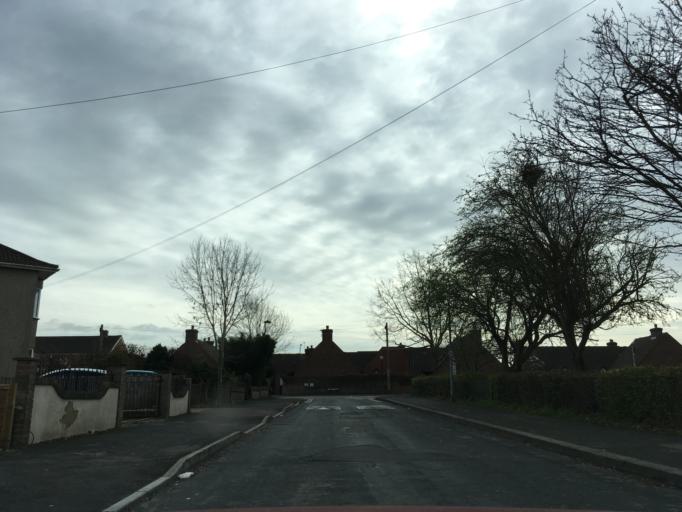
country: GB
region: England
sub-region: South Gloucestershire
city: Almondsbury
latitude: 51.5315
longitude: -2.5822
